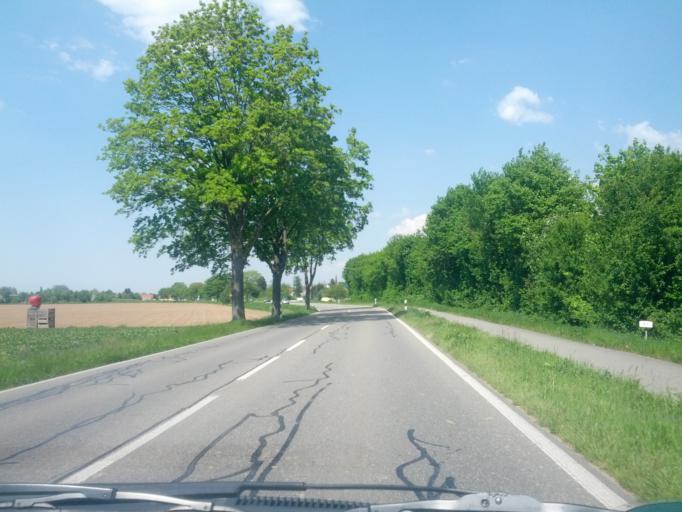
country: DE
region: Baden-Wuerttemberg
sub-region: Freiburg Region
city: Kenzingen
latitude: 48.1794
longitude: 7.7649
